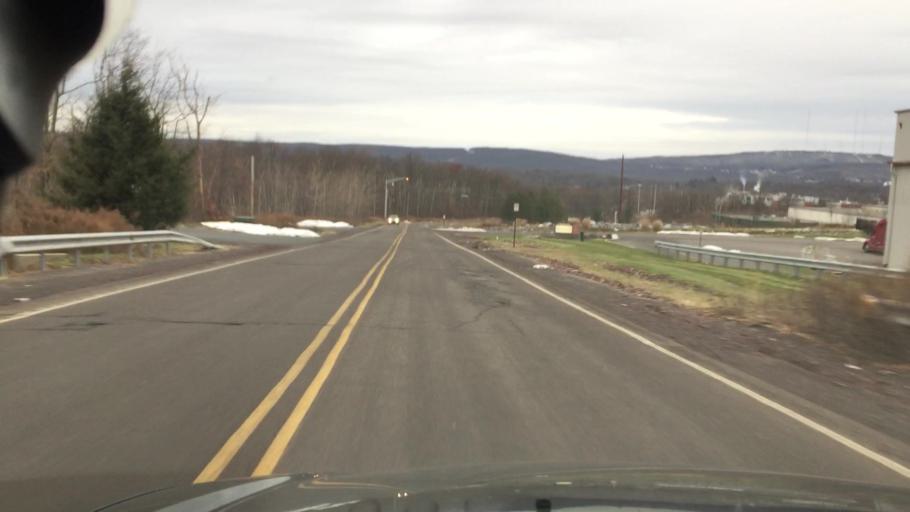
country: US
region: Pennsylvania
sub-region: Luzerne County
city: Mountain Top
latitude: 41.1353
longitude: -75.8982
